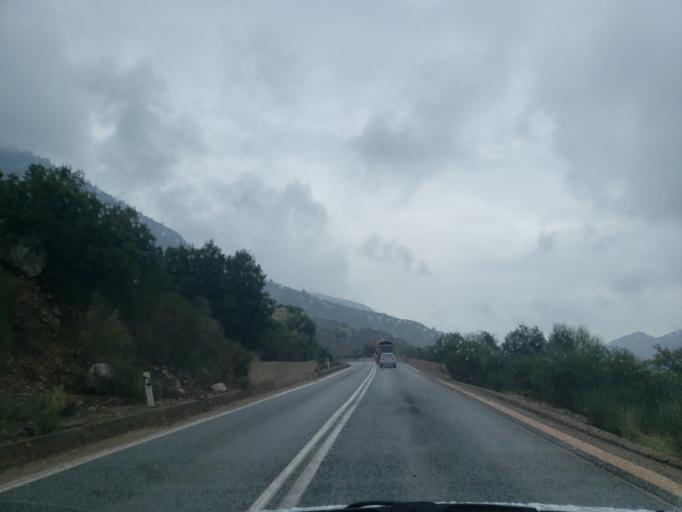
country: GR
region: Central Greece
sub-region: Nomos Fokidos
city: Amfissa
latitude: 38.5877
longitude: 22.3889
